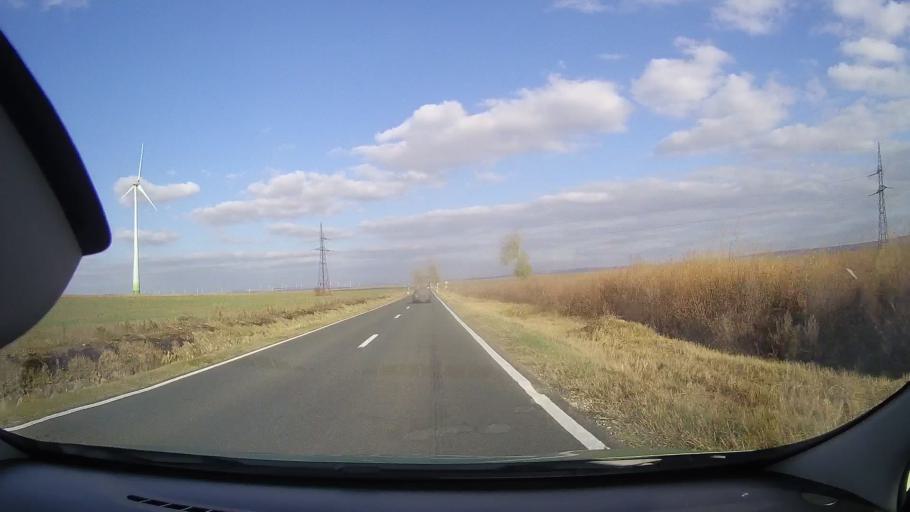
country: RO
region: Tulcea
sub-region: Comuna Topolog
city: Topolog
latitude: 44.8245
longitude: 28.2717
